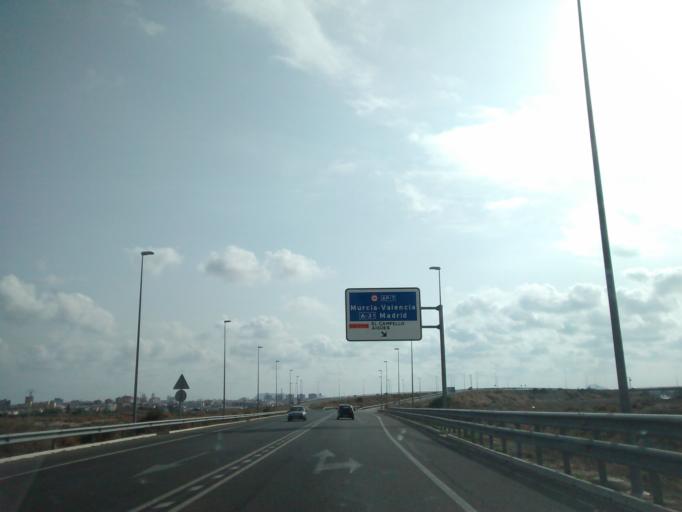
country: ES
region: Valencia
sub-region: Provincia de Alicante
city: el Campello
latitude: 38.4464
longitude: -0.3845
